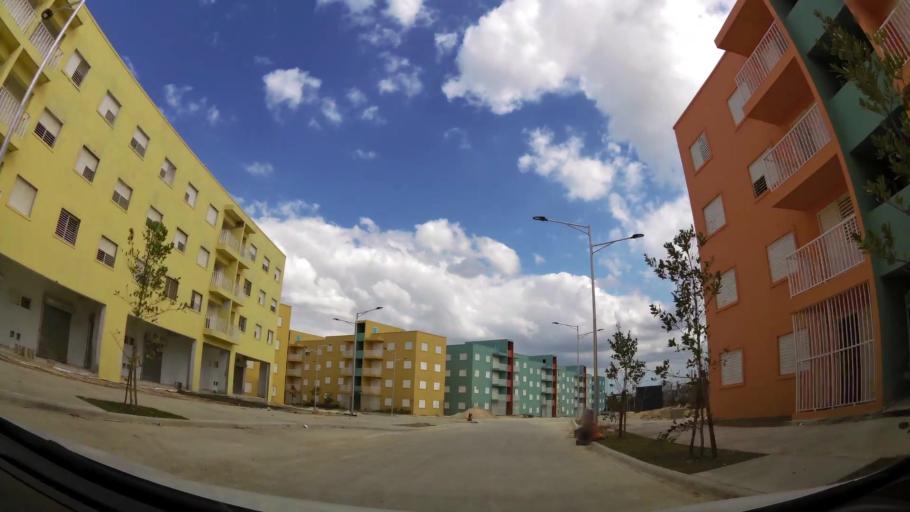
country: DO
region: Nacional
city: Ensanche Luperon
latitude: 18.5281
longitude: -69.8834
